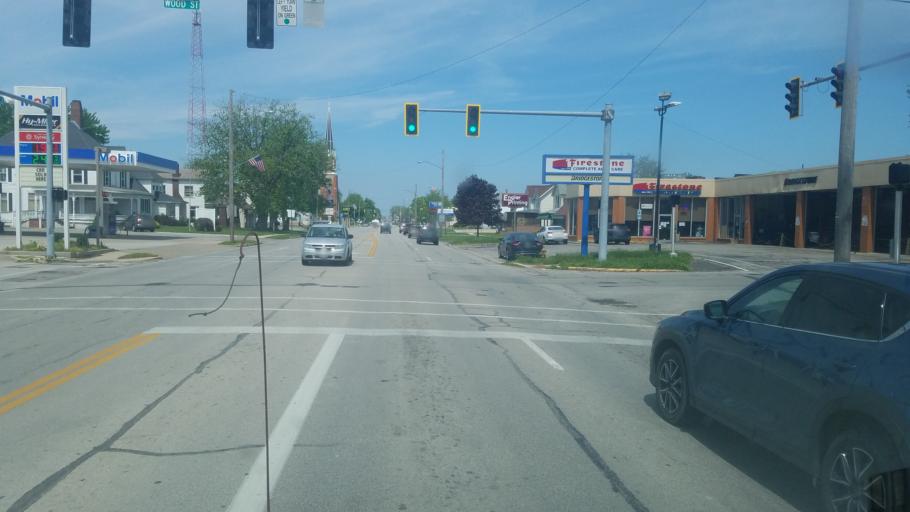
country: US
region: Ohio
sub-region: Sandusky County
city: Fremont
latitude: 41.3496
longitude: -83.1189
